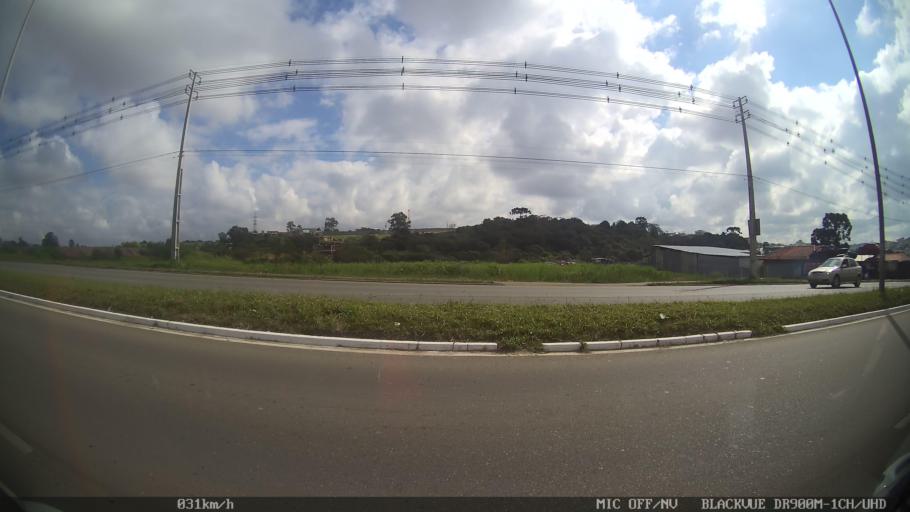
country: BR
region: Parana
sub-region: Pinhais
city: Pinhais
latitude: -25.3791
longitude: -49.1974
